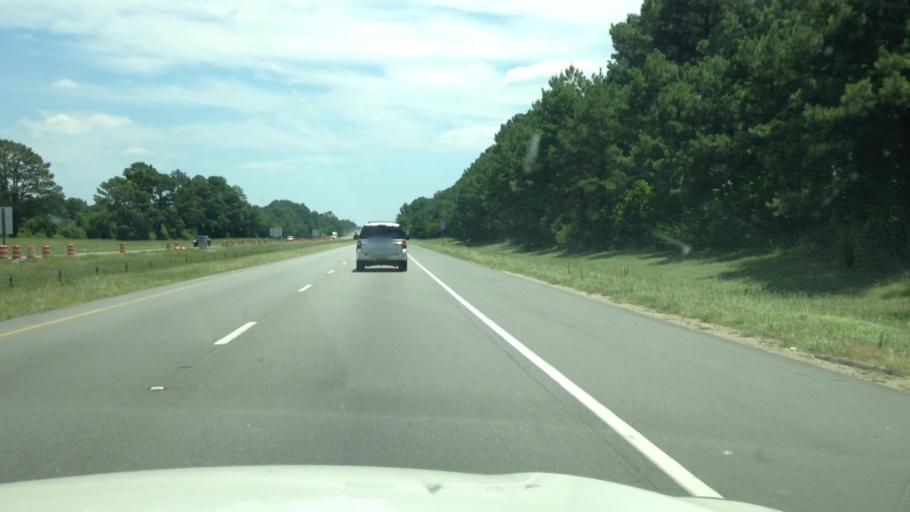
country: US
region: South Carolina
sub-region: Lee County
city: Bishopville
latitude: 34.1930
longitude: -80.2711
